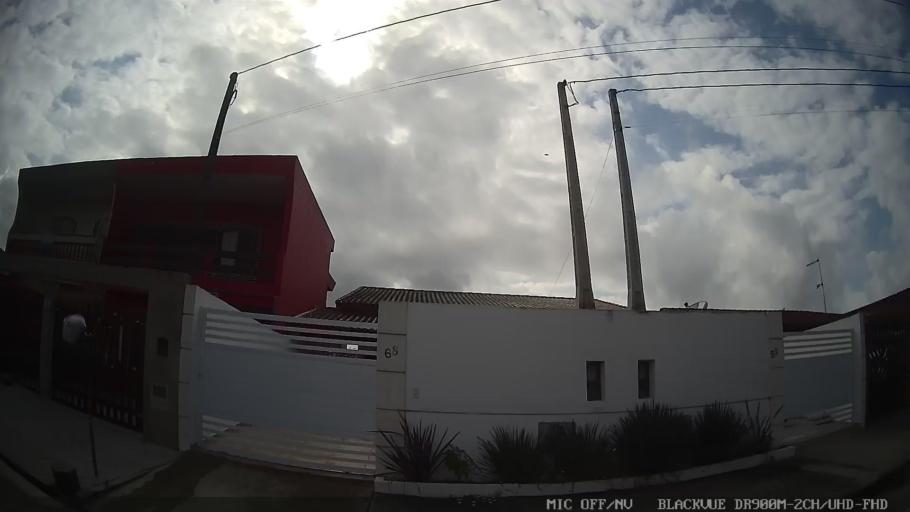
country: BR
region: Sao Paulo
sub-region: Itanhaem
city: Itanhaem
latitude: -24.2001
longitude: -46.8252
